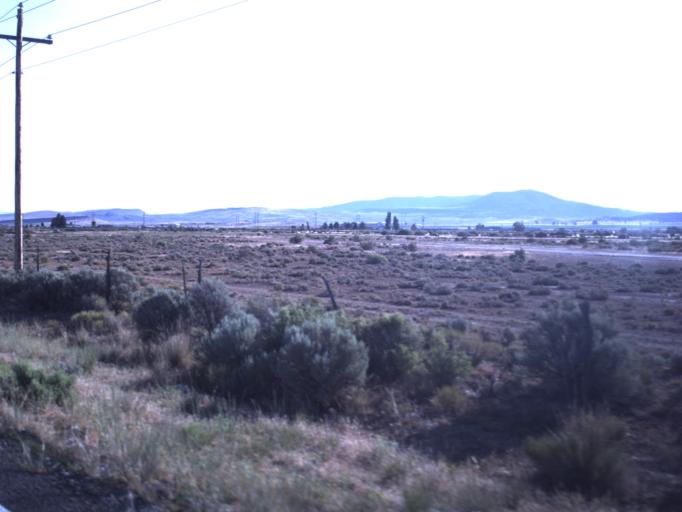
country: US
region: Utah
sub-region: Iron County
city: Enoch
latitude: 37.7912
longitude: -113.0506
